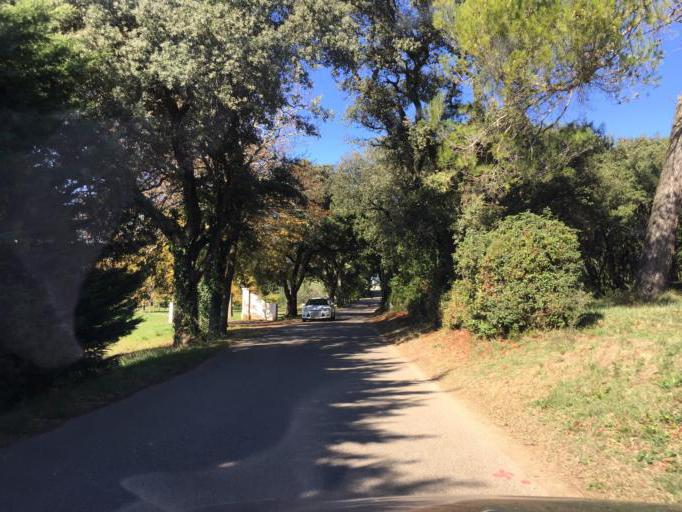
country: FR
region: Provence-Alpes-Cote d'Azur
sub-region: Departement du Vaucluse
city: Piolenc
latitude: 44.1706
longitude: 4.7882
